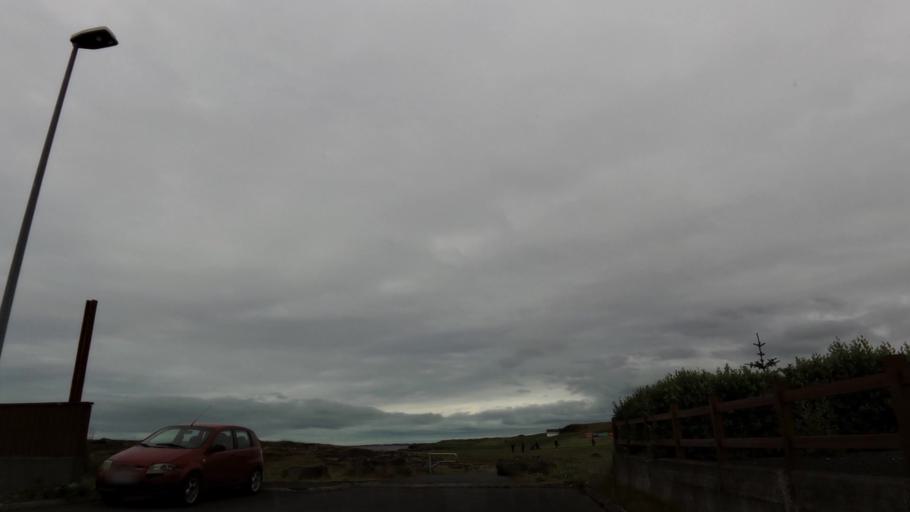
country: IS
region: Capital Region
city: Alftanes
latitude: 64.0566
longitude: -21.9935
